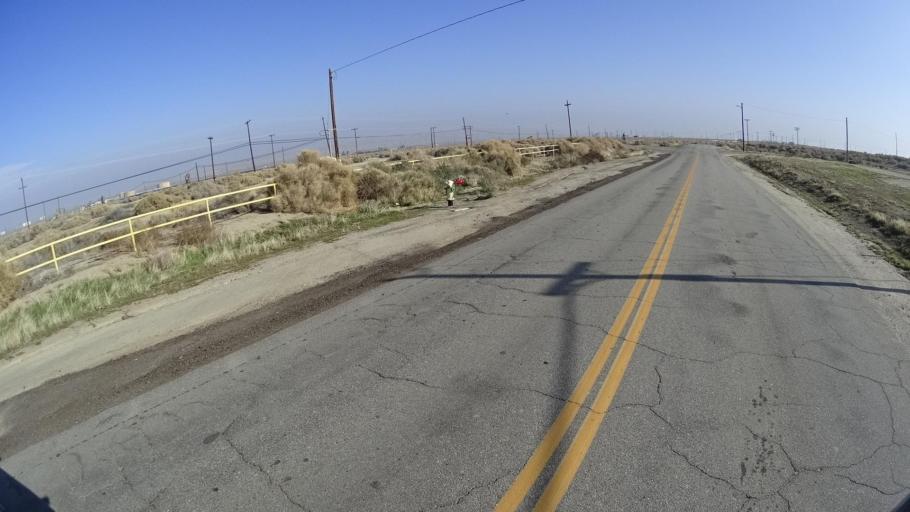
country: US
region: California
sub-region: Kern County
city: Taft Heights
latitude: 35.1795
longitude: -119.5413
